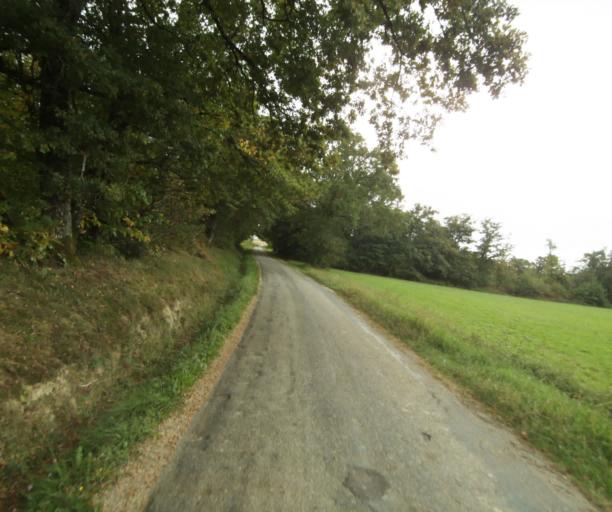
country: FR
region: Midi-Pyrenees
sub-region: Departement du Gers
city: Eauze
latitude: 43.8946
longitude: 0.1104
